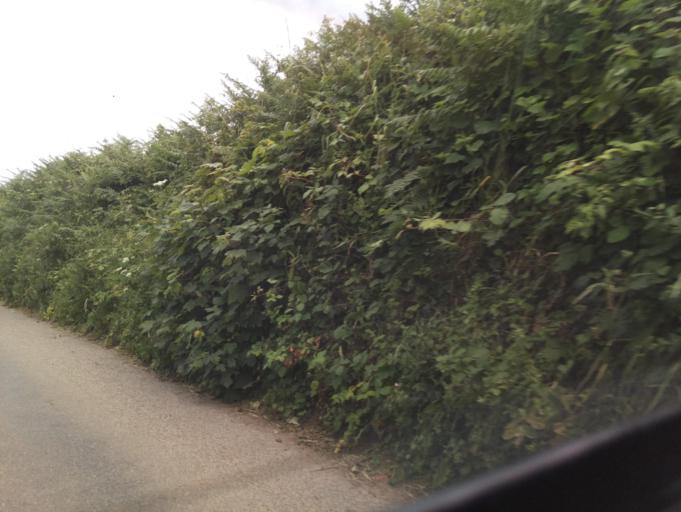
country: GB
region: England
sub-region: Devon
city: Dartmouth
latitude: 50.3616
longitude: -3.6370
